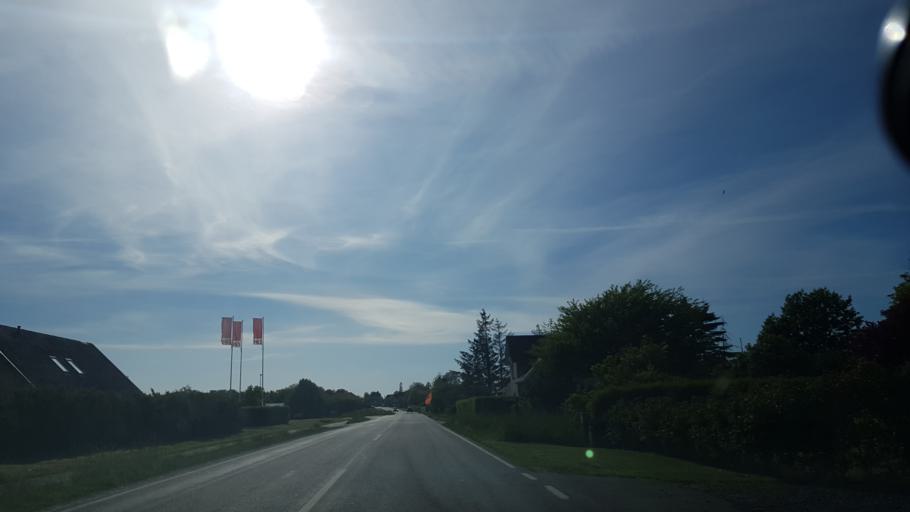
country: DK
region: Zealand
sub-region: Slagelse Kommune
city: Forlev
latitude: 55.4368
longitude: 11.2560
